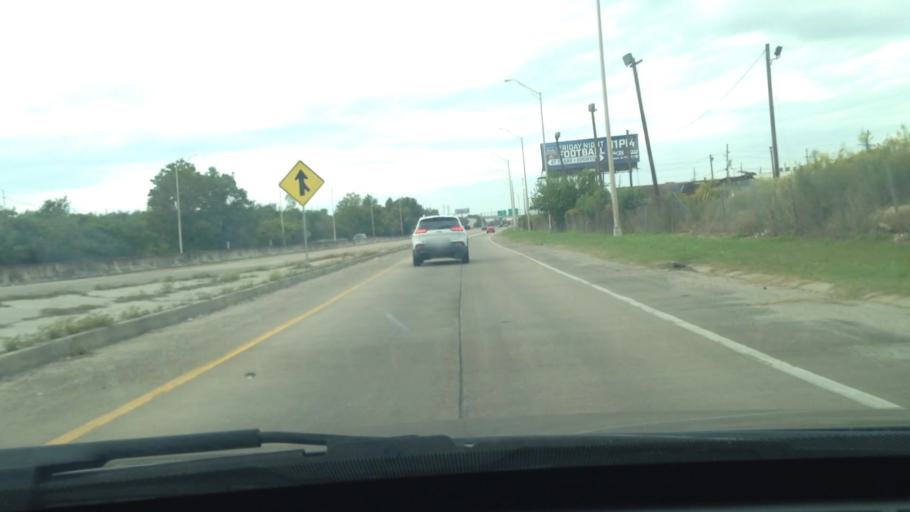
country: US
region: Louisiana
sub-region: Jefferson Parish
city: Jefferson
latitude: 29.9695
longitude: -90.1352
